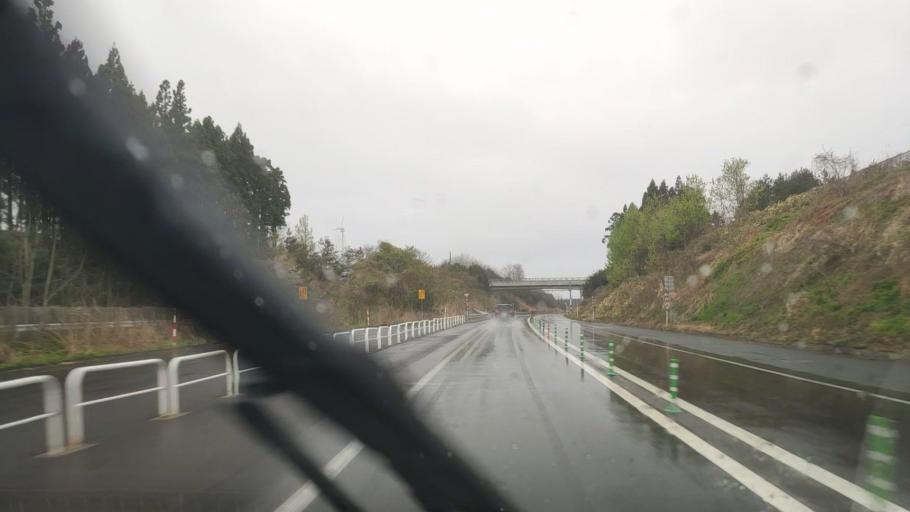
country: JP
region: Akita
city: Noshiromachi
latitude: 40.1624
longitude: 140.0417
